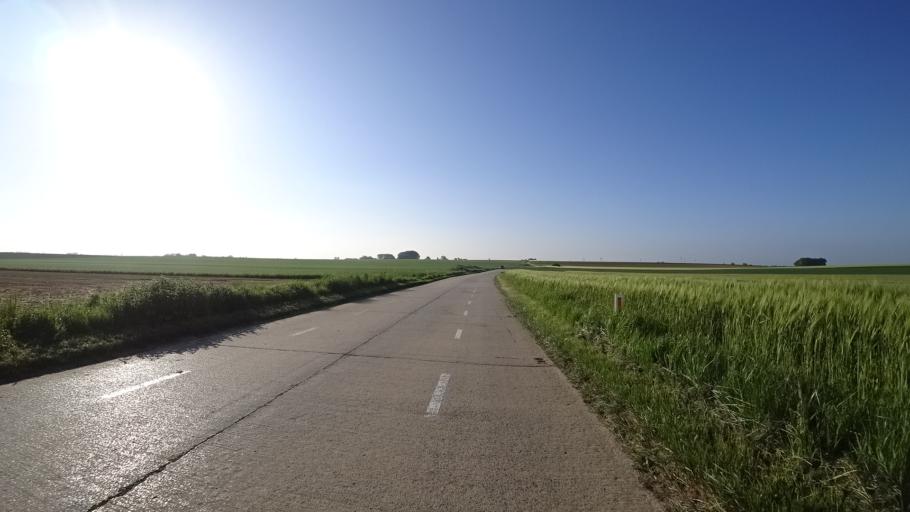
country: BE
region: Wallonia
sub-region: Province du Brabant Wallon
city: Walhain-Saint-Paul
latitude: 50.6341
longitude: 4.6809
